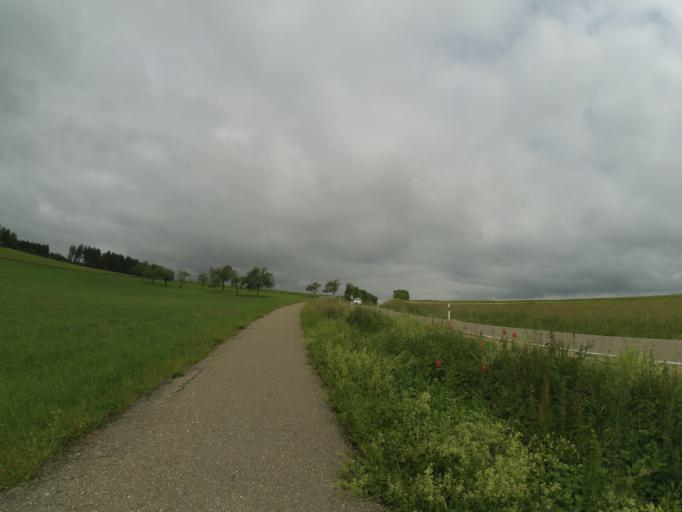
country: DE
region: Baden-Wuerttemberg
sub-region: Tuebingen Region
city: Bernstadt
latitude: 48.4895
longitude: 10.0315
